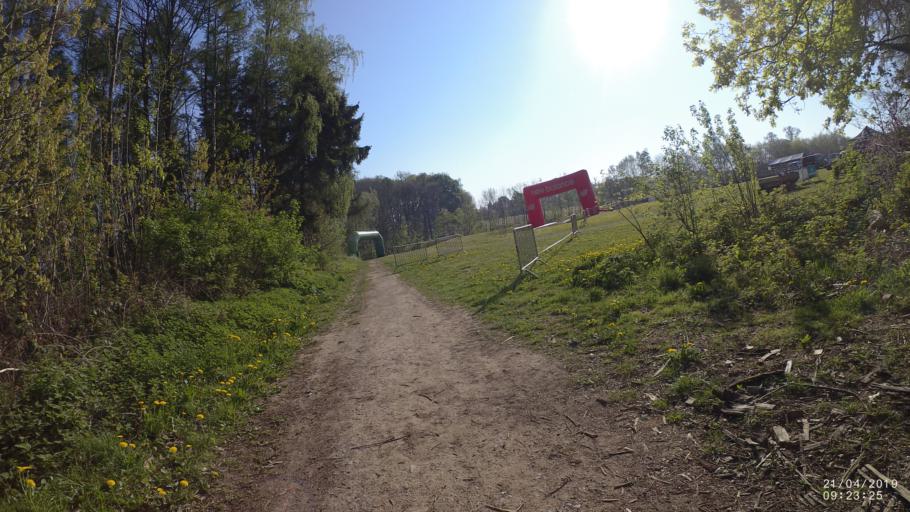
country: BE
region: Flanders
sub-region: Provincie Vlaams-Brabant
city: Lubbeek
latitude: 50.9193
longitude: 4.8535
